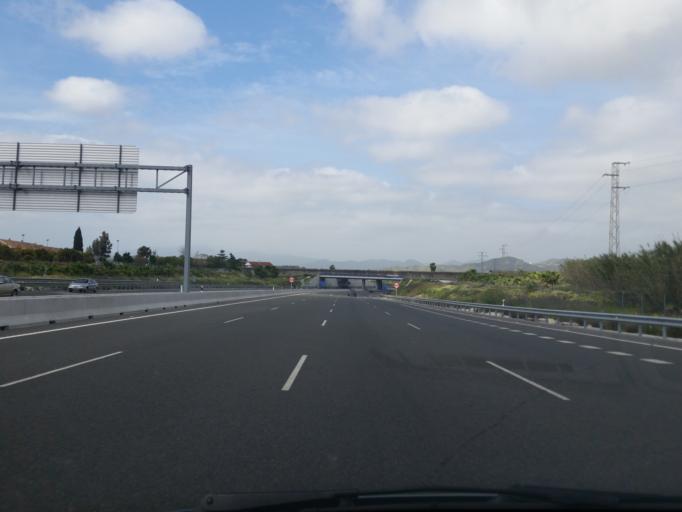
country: ES
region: Andalusia
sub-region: Provincia de Malaga
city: Alhaurin de la Torre
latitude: 36.6836
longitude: -4.5263
